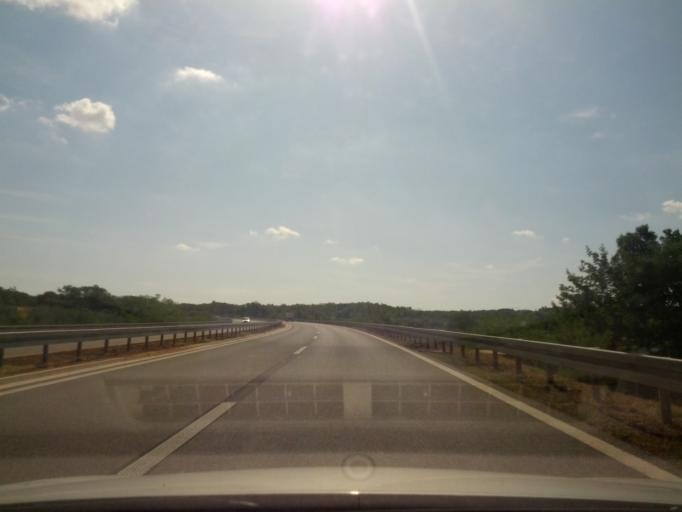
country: HR
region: Istarska
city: Buje
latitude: 45.3199
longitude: 13.6781
